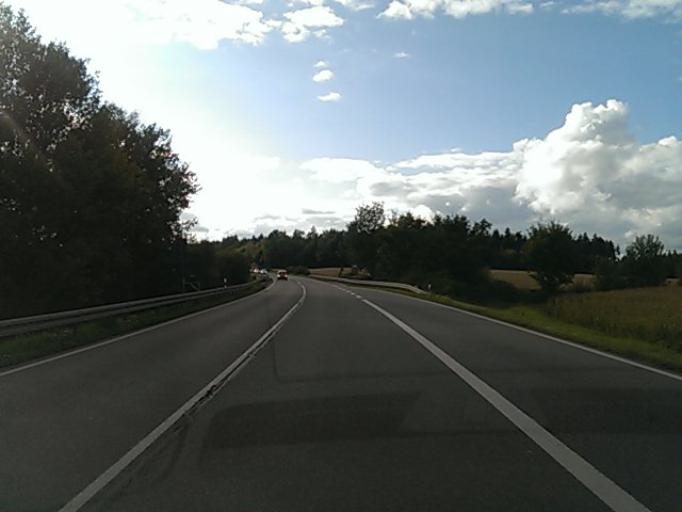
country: DE
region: Baden-Wuerttemberg
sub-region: Freiburg Region
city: Zimmern ob Rottweil
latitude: 48.1762
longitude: 8.5982
